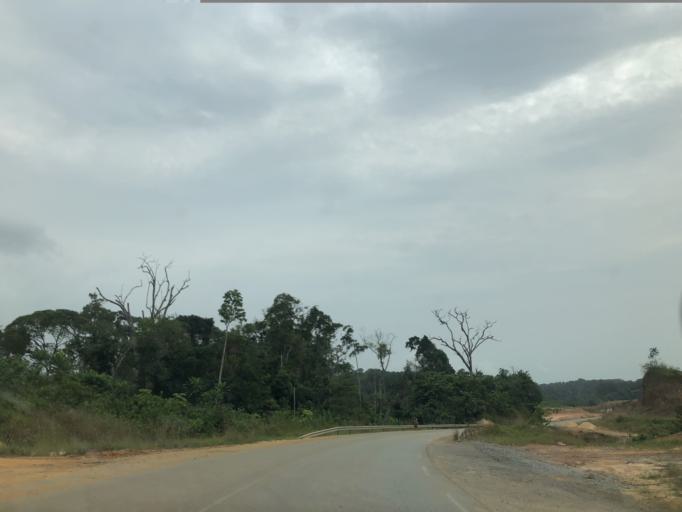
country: CM
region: South Province
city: Kribi
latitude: 2.7212
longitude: 9.8697
